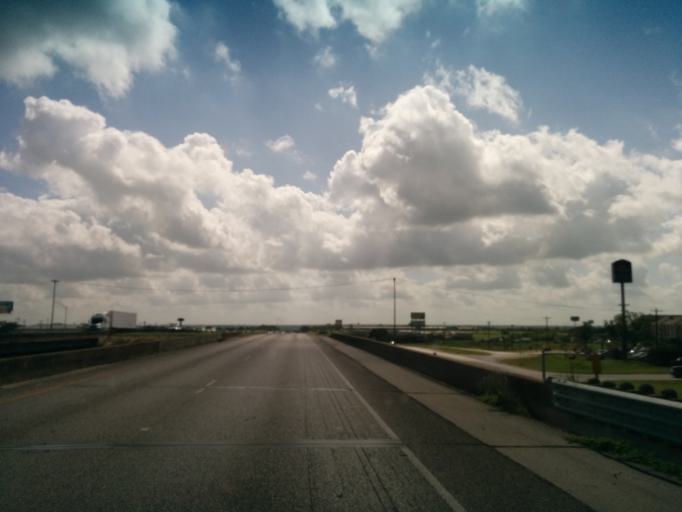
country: US
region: Texas
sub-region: Fayette County
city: Schulenburg
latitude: 29.6932
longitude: -96.9032
